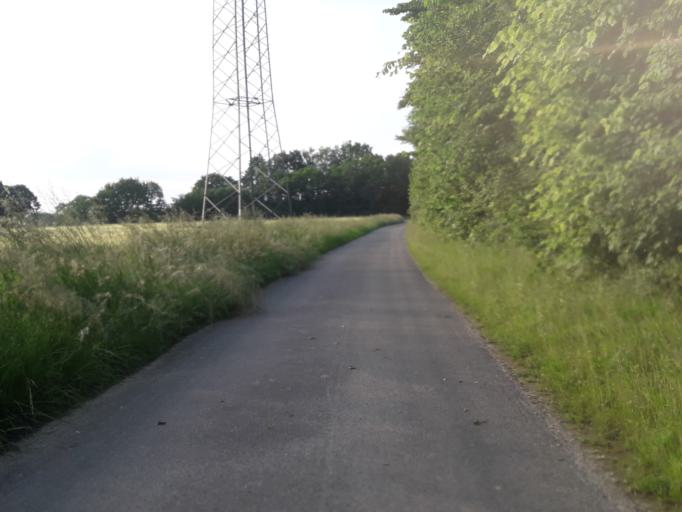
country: DE
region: North Rhine-Westphalia
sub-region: Regierungsbezirk Detmold
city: Salzkotten
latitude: 51.6779
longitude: 8.6487
